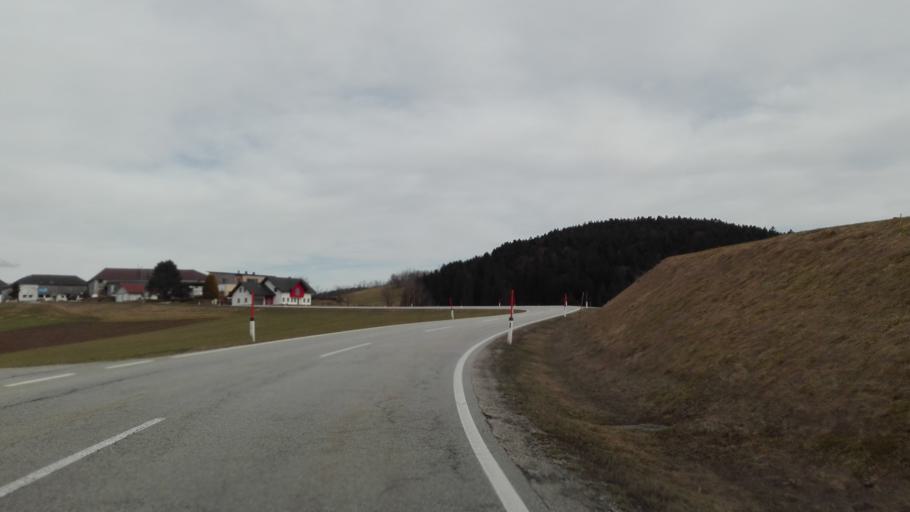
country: DE
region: Bavaria
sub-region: Lower Bavaria
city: Wegscheid
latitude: 48.6040
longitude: 13.8137
